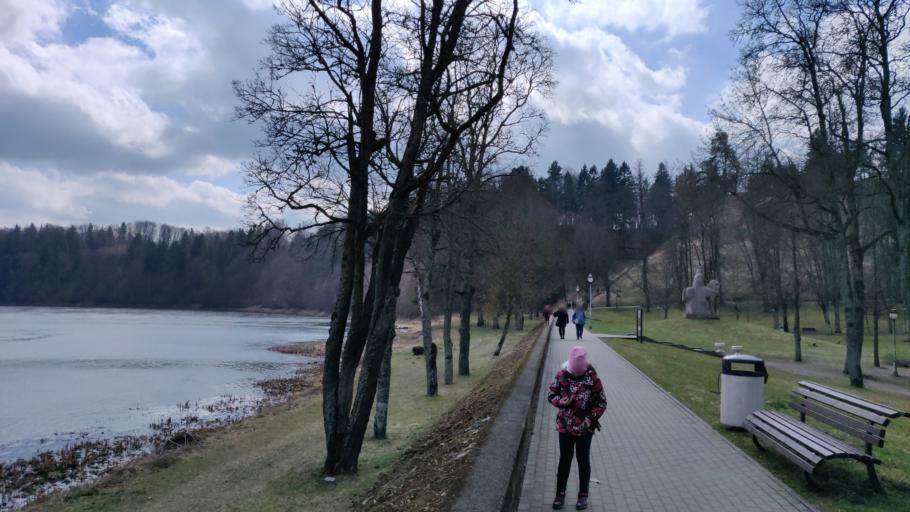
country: LT
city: Birstonas
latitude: 54.5989
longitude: 24.0355
